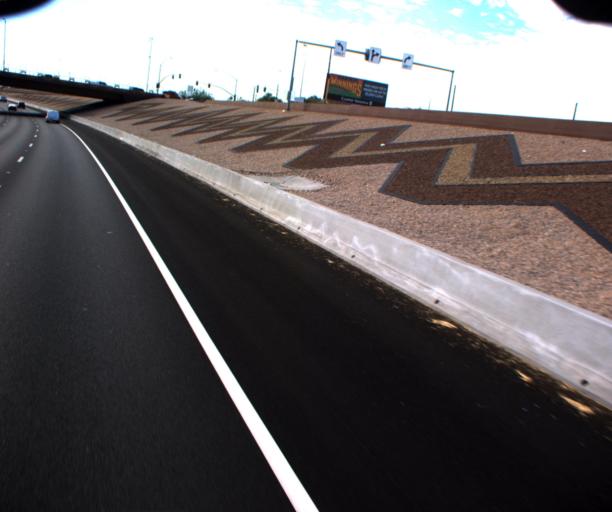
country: US
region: Arizona
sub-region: Maricopa County
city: Scottsdale
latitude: 33.4817
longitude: -111.8900
